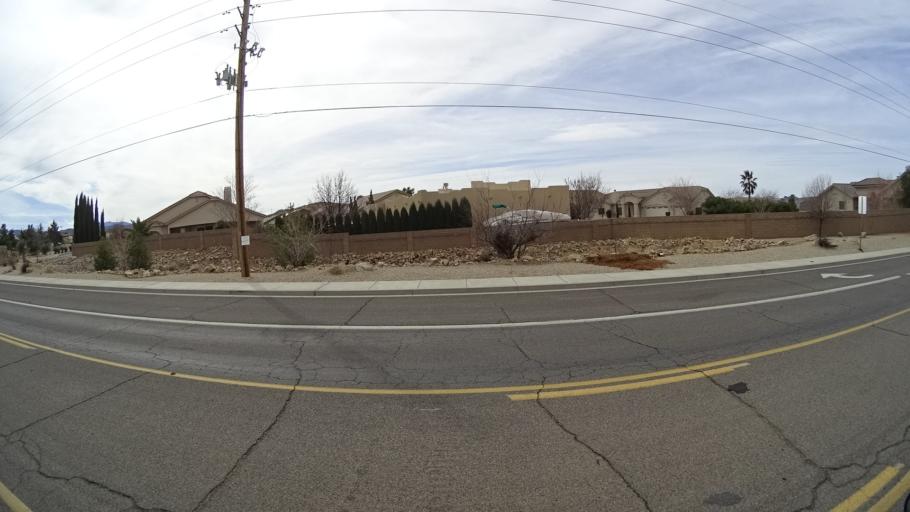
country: US
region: Arizona
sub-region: Mohave County
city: Kingman
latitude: 35.1867
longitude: -114.0075
